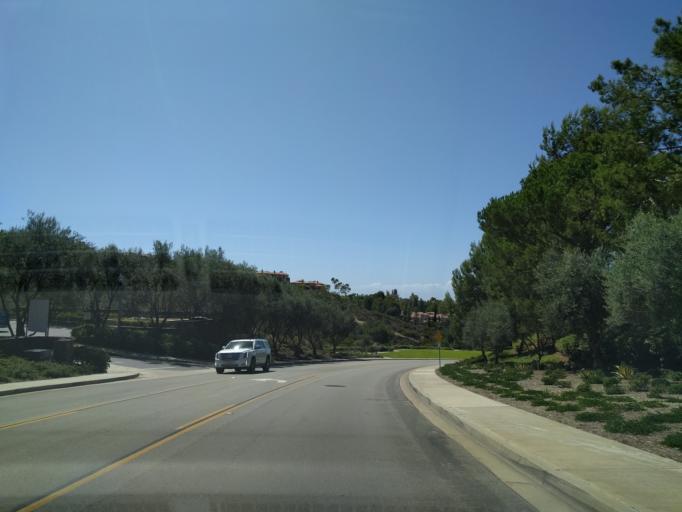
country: US
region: California
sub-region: Orange County
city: San Joaquin Hills
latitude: 33.6055
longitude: -117.8219
